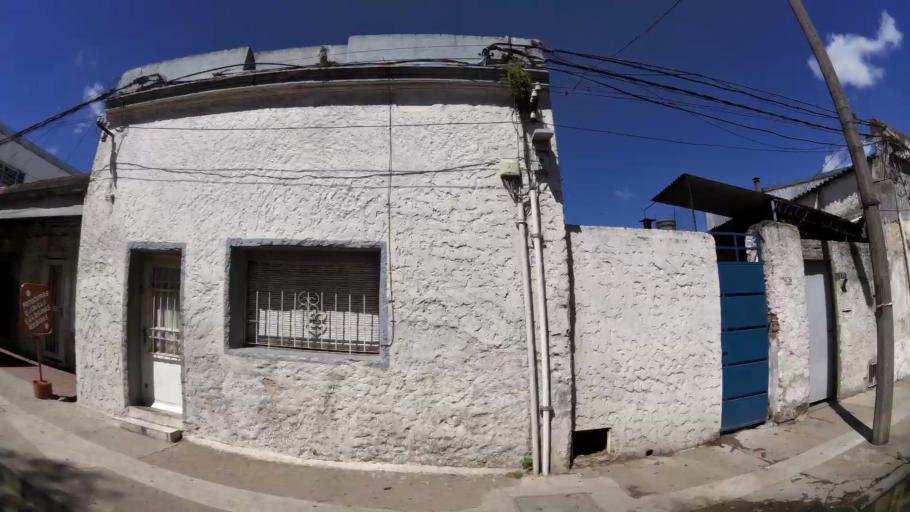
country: UY
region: Montevideo
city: Montevideo
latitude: -34.8407
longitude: -56.1452
